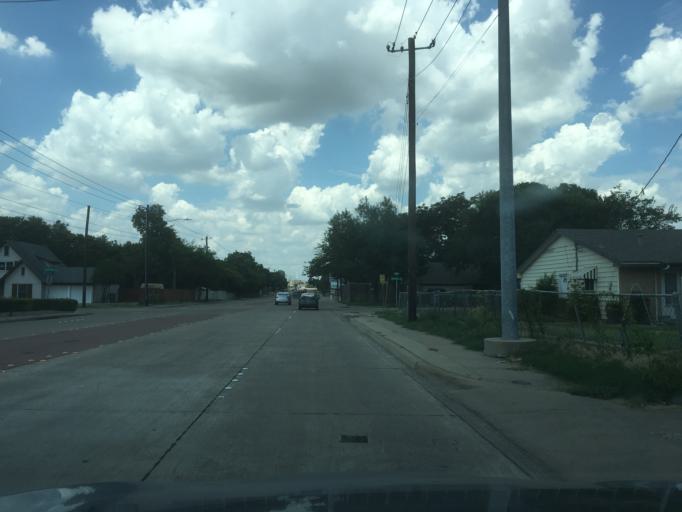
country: US
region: Texas
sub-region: Dallas County
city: Garland
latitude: 32.8714
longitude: -96.6482
